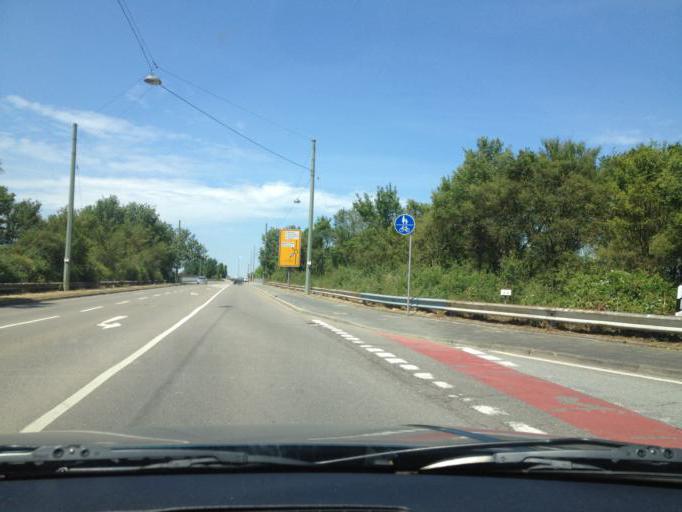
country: DE
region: Rheinland-Pfalz
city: Gartenstadt
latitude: 49.4443
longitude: 8.4118
